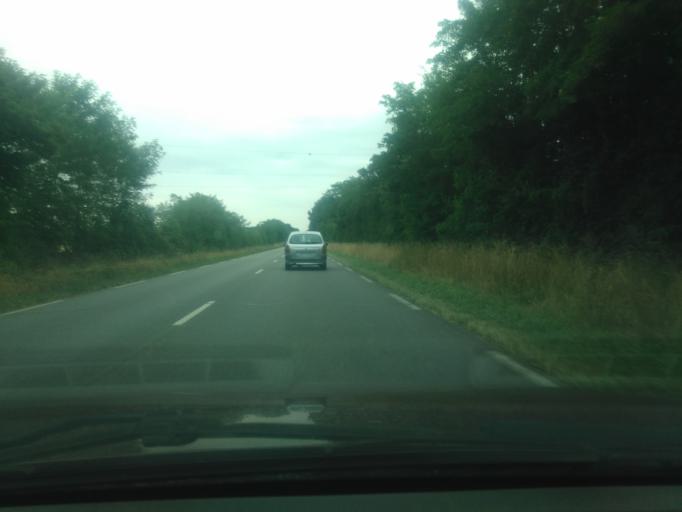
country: FR
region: Centre
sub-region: Departement de l'Indre
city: Le Blanc
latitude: 46.6160
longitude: 1.0173
